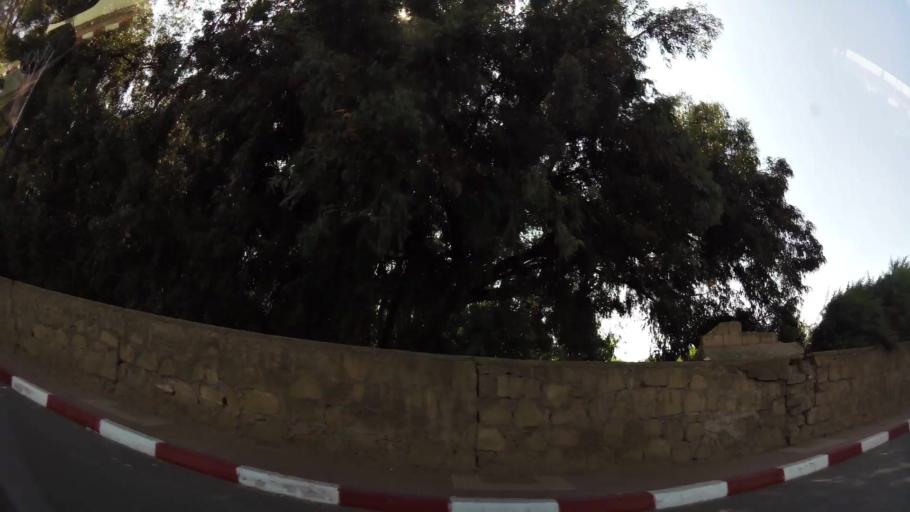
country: MA
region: Rabat-Sale-Zemmour-Zaer
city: Sale
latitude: 34.0392
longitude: -6.7752
